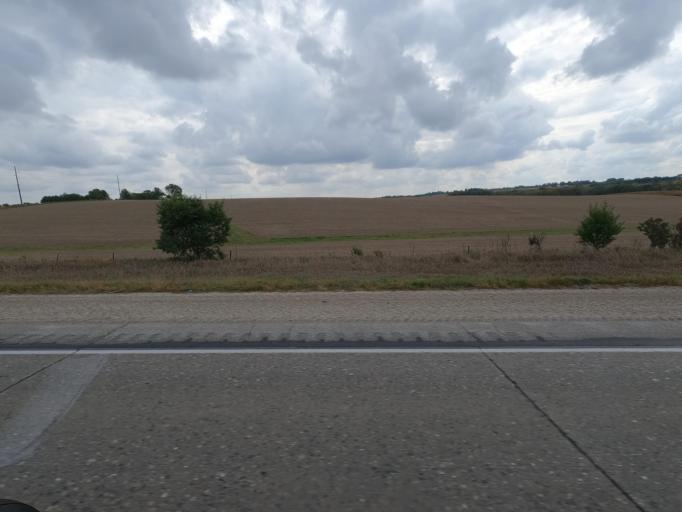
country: US
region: Iowa
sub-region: Polk County
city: Mitchellville
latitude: 41.6006
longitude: -93.3981
